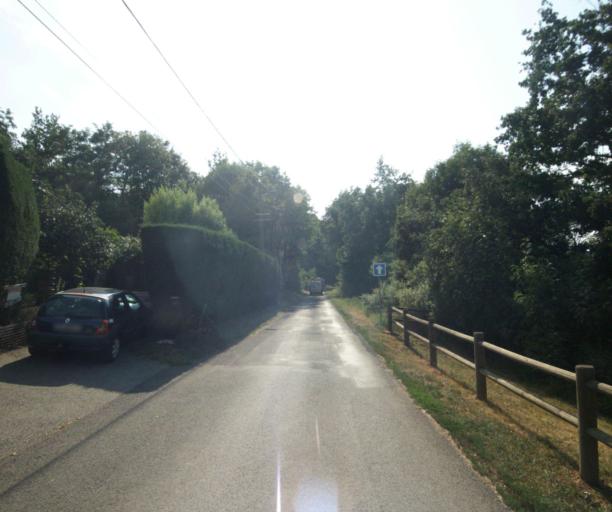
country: FR
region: Rhone-Alpes
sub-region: Departement du Rhone
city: Saint-Germain-Nuelles
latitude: 45.8359
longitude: 4.6089
